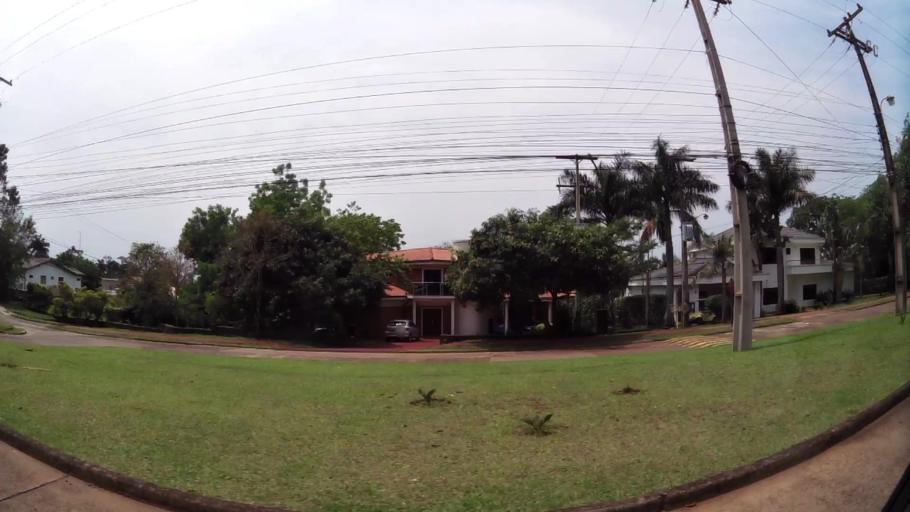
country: PY
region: Alto Parana
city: Ciudad del Este
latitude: -25.4950
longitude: -54.6111
